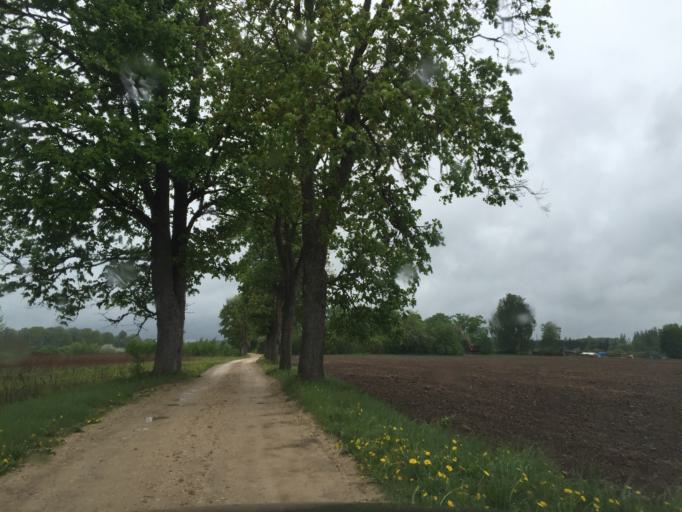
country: LV
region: Ogre
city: Jumprava
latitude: 56.6643
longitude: 25.0014
